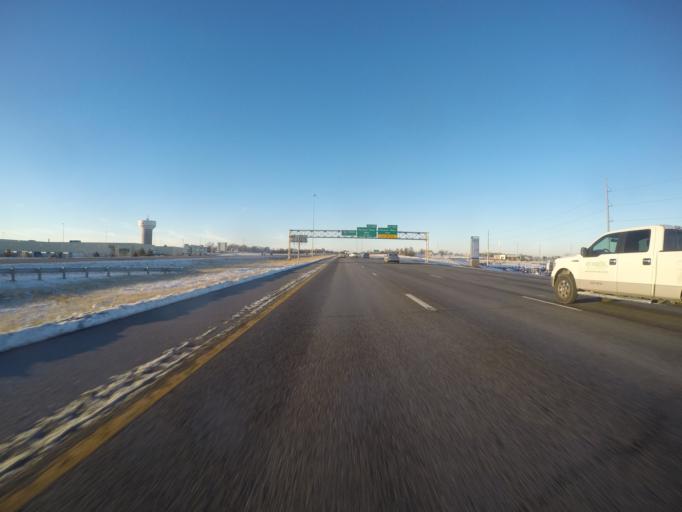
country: US
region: Kansas
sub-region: Wyandotte County
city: Edwardsville
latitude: 39.1238
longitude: -94.8140
